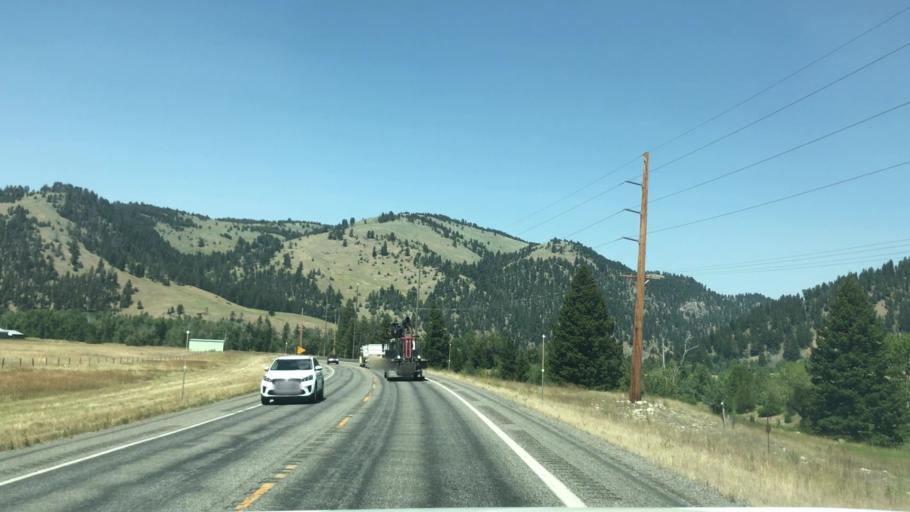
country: US
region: Montana
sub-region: Gallatin County
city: Four Corners
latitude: 45.4880
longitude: -111.2709
